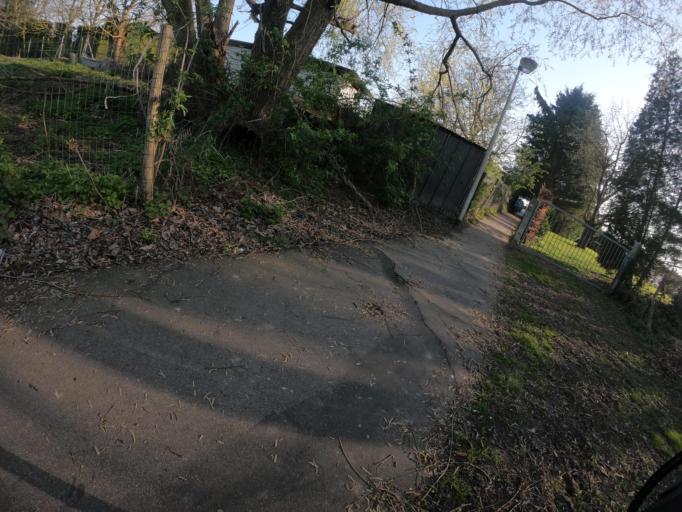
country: BE
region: Flanders
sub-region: Provincie Limburg
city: Heers
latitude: 50.8078
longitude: 5.2834
